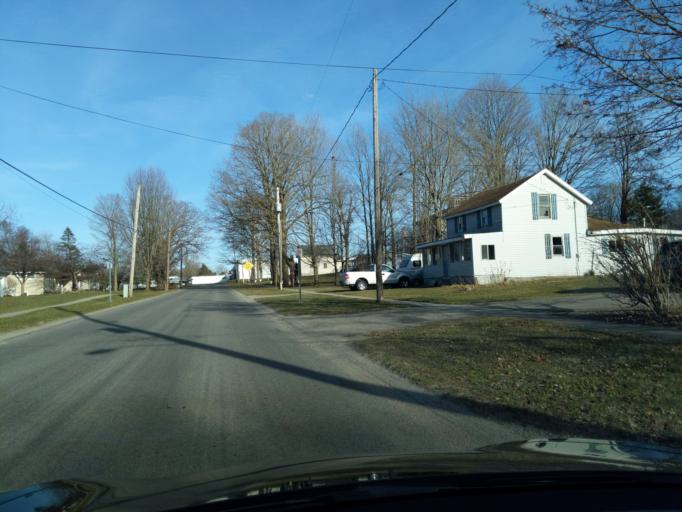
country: US
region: Michigan
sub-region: Ionia County
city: Saranac
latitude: 42.9313
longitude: -85.2055
